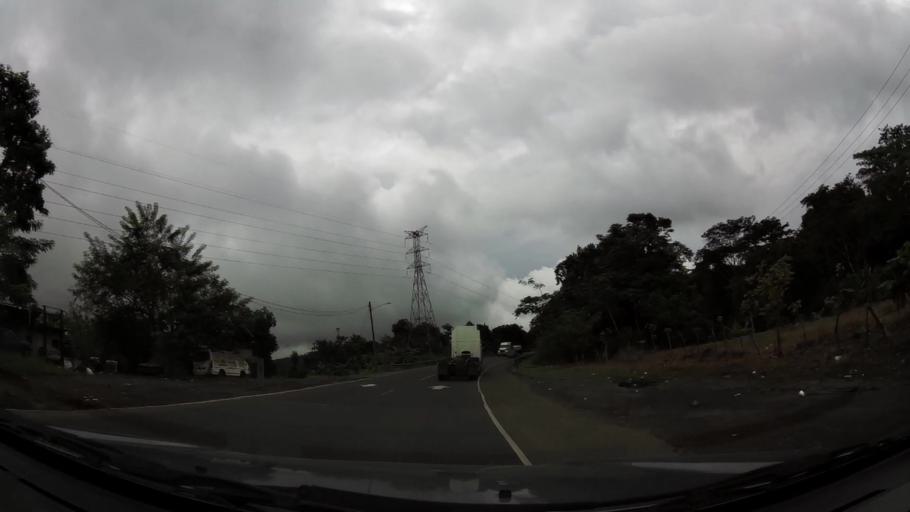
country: PA
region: Colon
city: Nuevo San Juan
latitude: 9.2021
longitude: -79.6263
